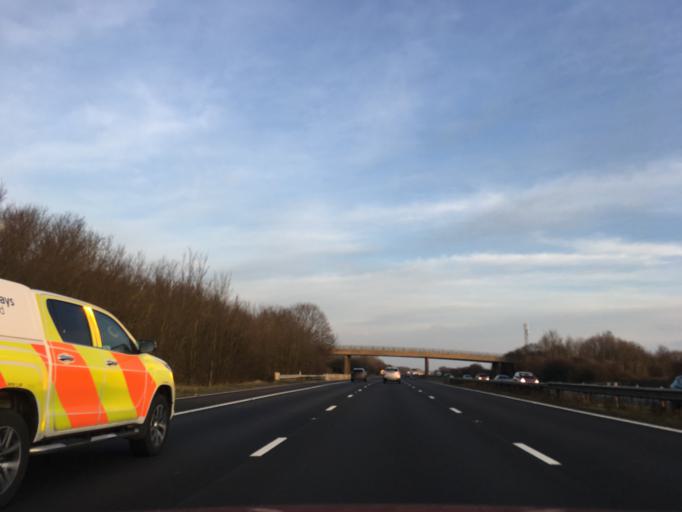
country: GB
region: England
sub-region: Gloucestershire
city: Tewkesbury
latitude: 51.9656
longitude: -2.1286
